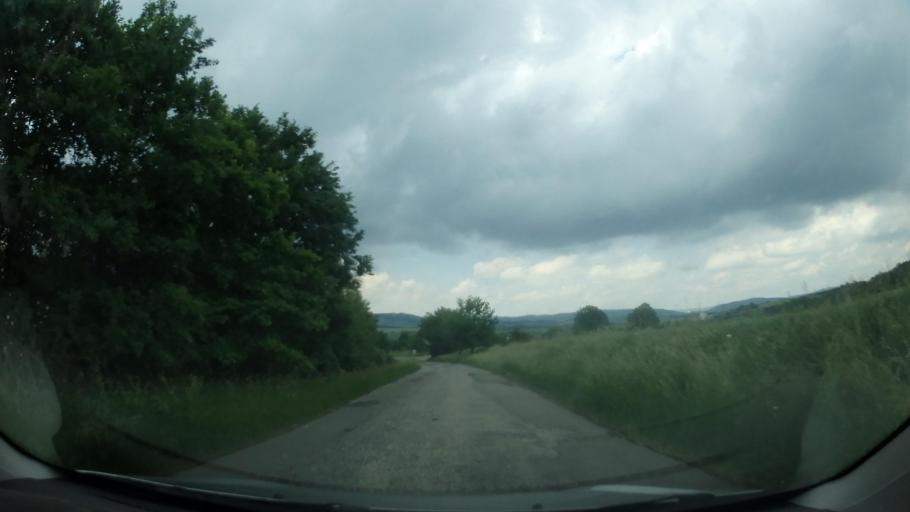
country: CZ
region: South Moravian
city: Doubravice nad Svitavou
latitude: 49.4627
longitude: 16.6052
